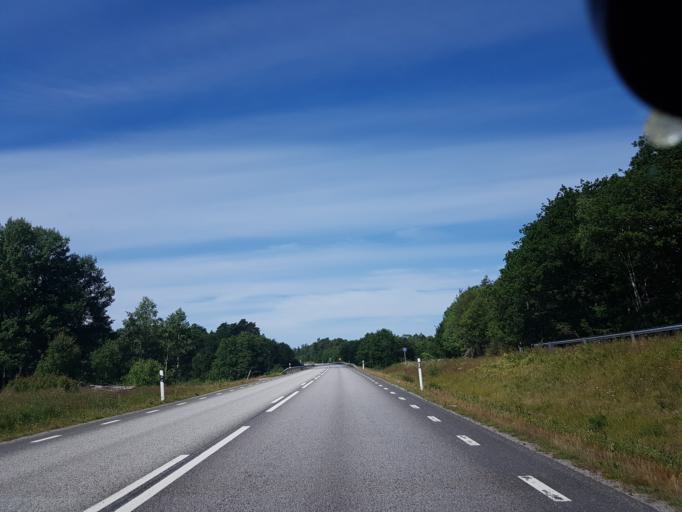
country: SE
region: Vaestra Goetaland
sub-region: Orust
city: Henan
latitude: 58.1552
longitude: 11.5484
